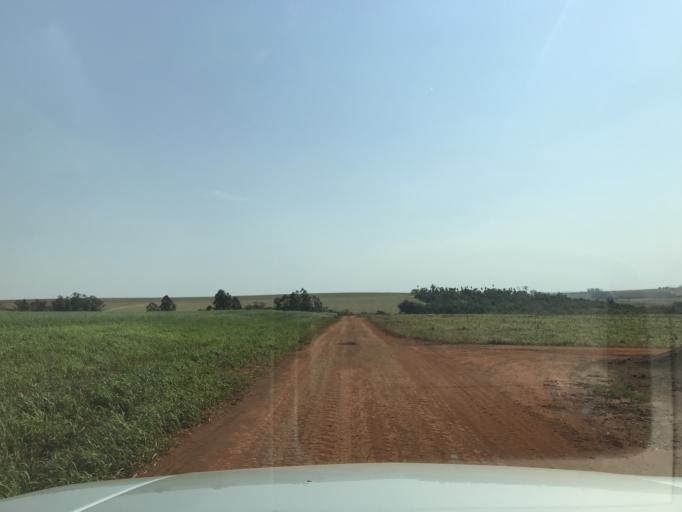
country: BR
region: Parana
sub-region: Palotina
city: Palotina
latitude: -24.2271
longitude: -53.7385
